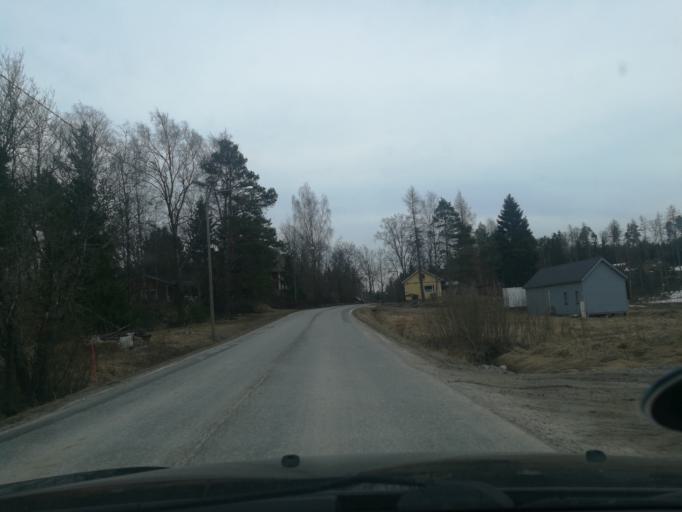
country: FI
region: Uusimaa
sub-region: Helsinki
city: Nickby
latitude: 60.2817
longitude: 25.3715
